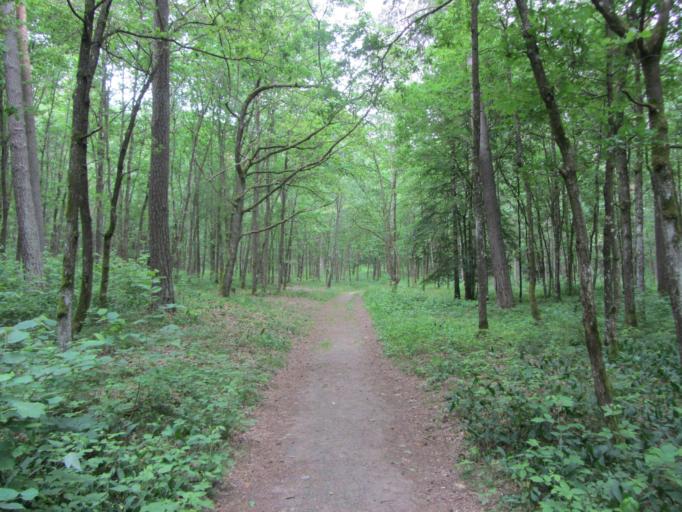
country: LT
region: Vilnius County
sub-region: Vilniaus Rajonas
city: Vievis
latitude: 54.8131
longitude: 24.9632
